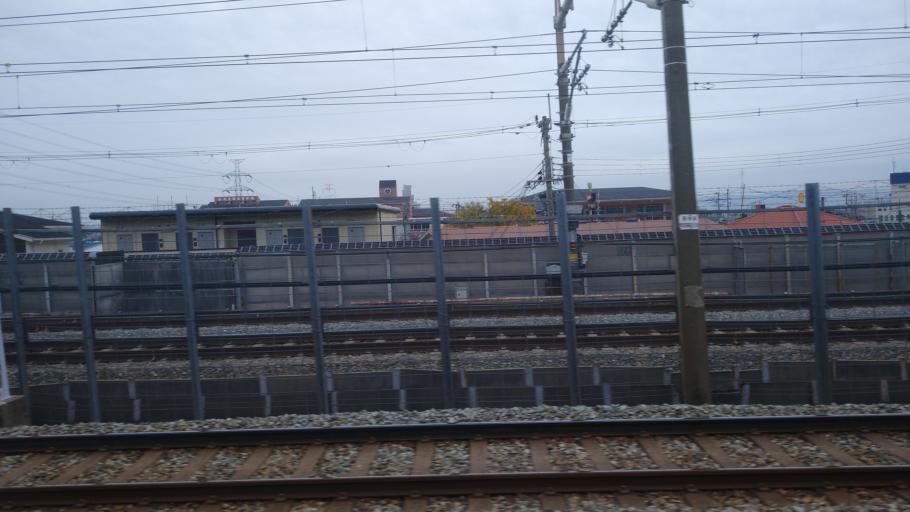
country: JP
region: Kyoto
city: Yawata
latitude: 34.8713
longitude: 135.6609
